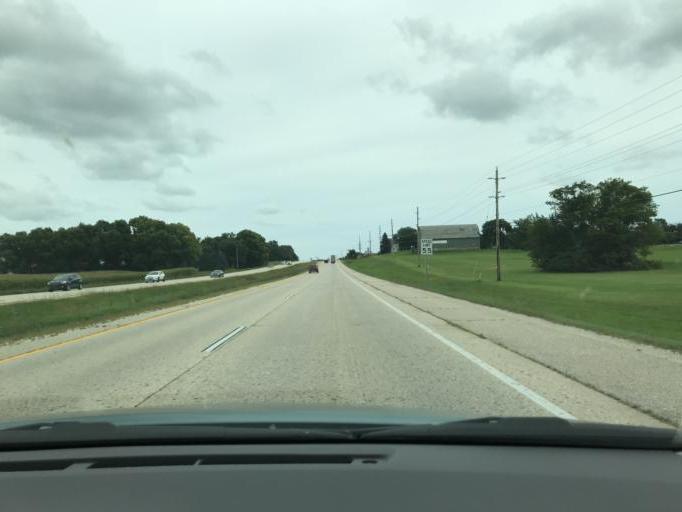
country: US
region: Wisconsin
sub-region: Kenosha County
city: Bristol
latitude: 42.5679
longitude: -88.0159
